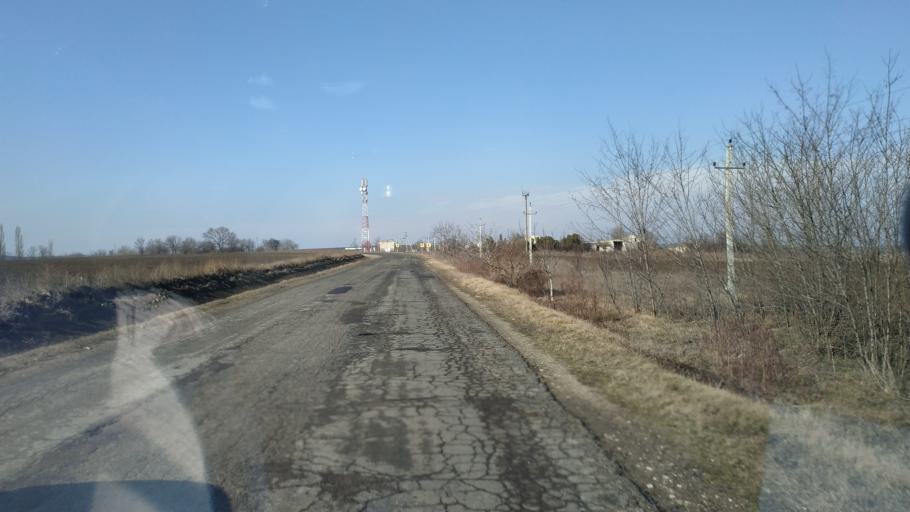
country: MD
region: Chisinau
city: Singera
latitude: 46.6971
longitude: 29.0582
